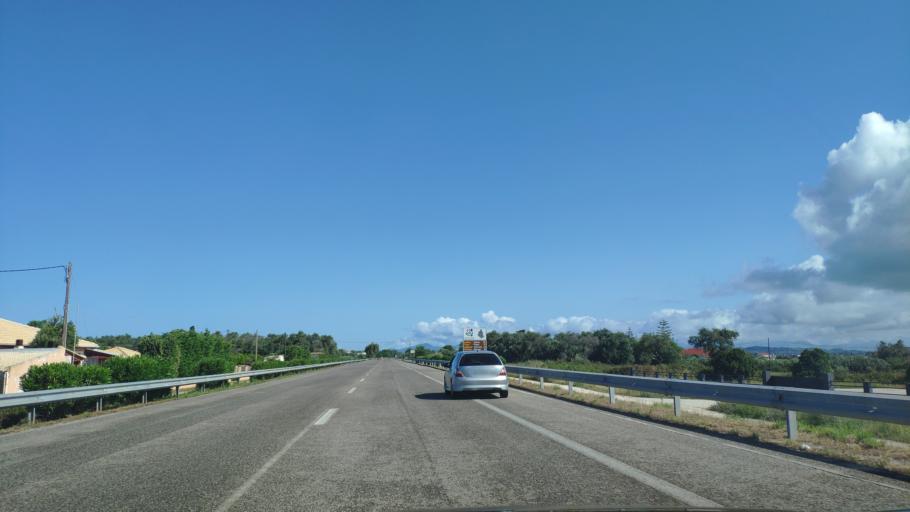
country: GR
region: Epirus
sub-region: Nomos Prevezis
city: Preveza
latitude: 38.9524
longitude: 20.7334
